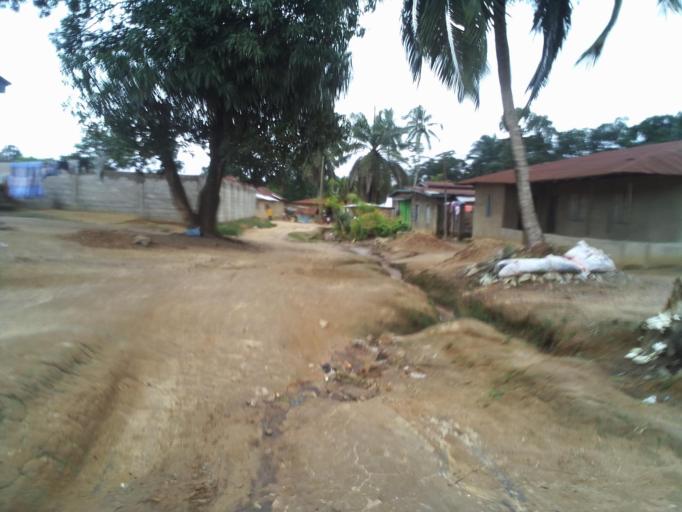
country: SL
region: Eastern Province
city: Kenema
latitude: 7.8578
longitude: -11.1861
